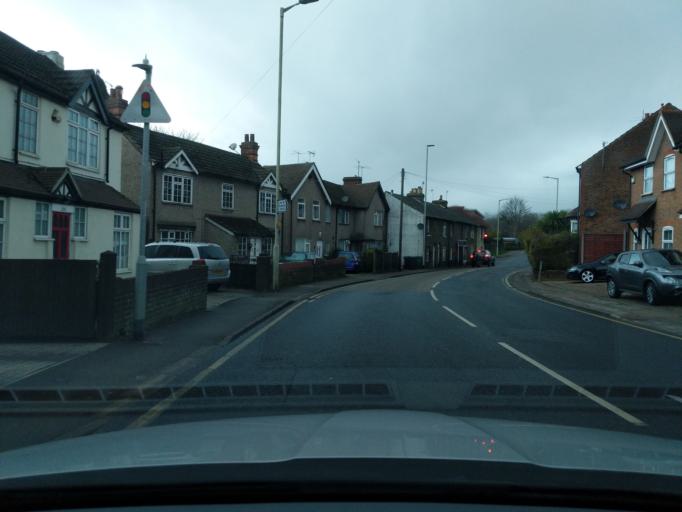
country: GB
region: England
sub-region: Hertfordshire
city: Hemel Hempstead
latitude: 51.7402
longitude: -0.4666
